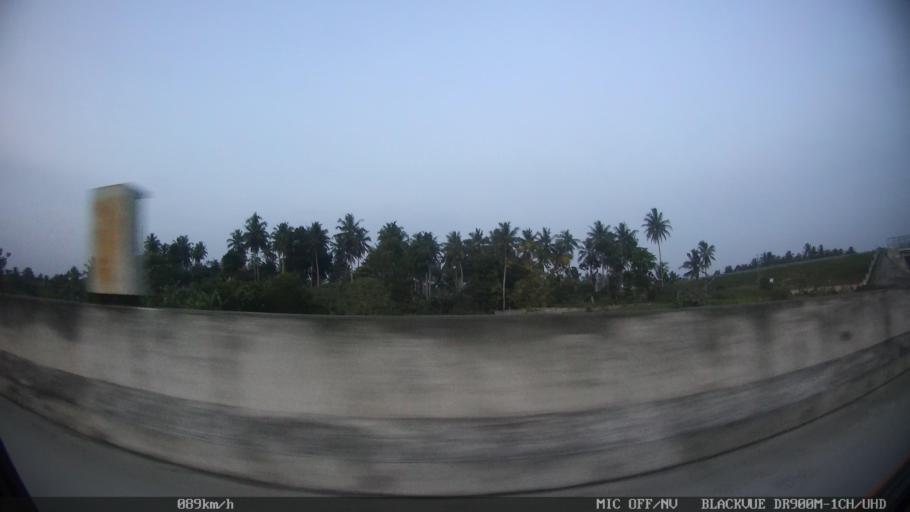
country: ID
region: Lampung
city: Sidorejo
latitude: -5.6477
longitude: 105.5802
